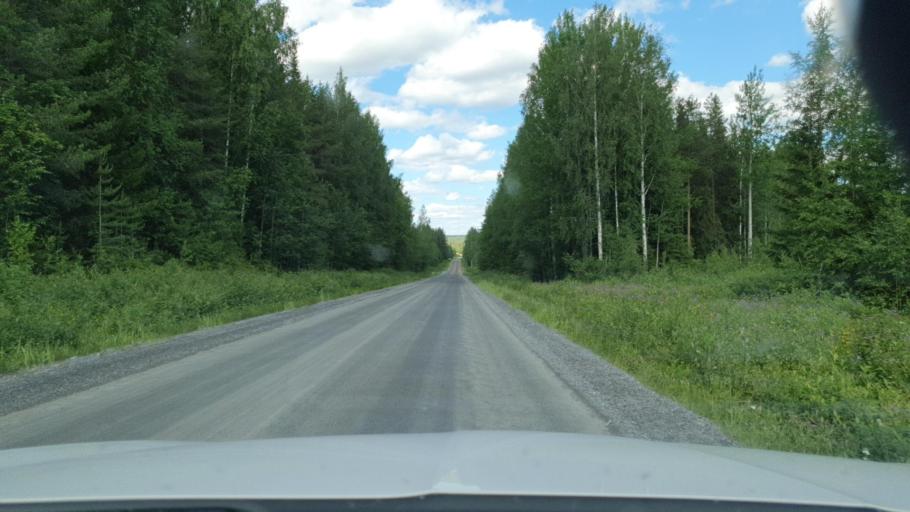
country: SE
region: Vaesterbotten
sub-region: Skelleftea Kommun
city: Forsbacka
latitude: 64.8317
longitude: 20.5013
